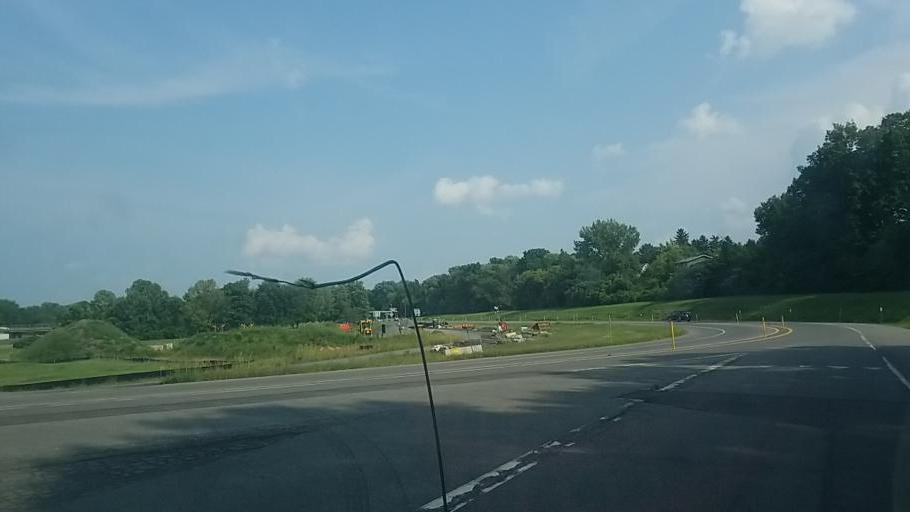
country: US
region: New York
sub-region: Onondaga County
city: Liverpool
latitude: 43.1158
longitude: -76.2192
